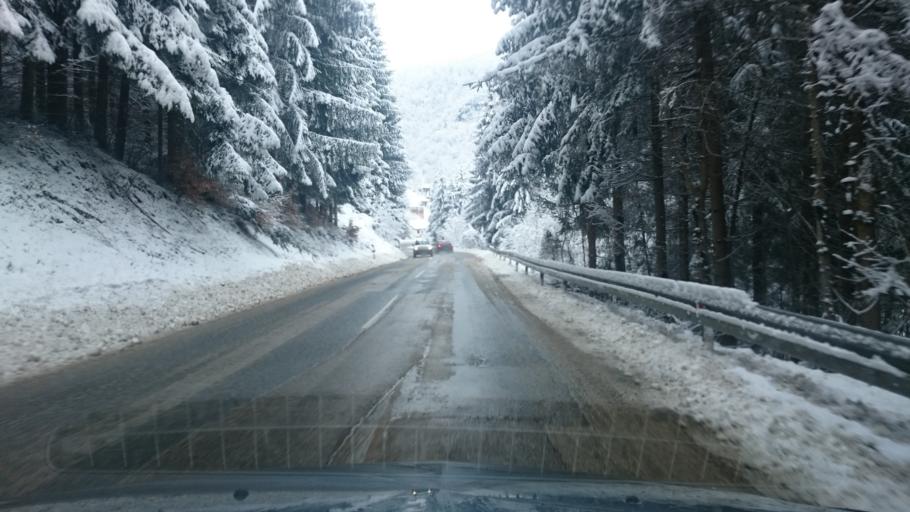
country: BA
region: Republika Srpska
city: Zivinice
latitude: 44.5172
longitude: 17.3028
